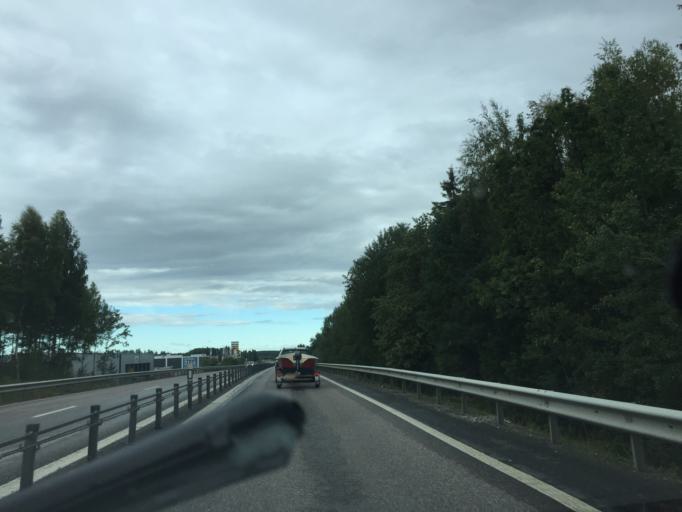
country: SE
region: Soedermanland
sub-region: Eskilstuna Kommun
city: Hallbybrunn
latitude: 59.4002
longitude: 16.4331
